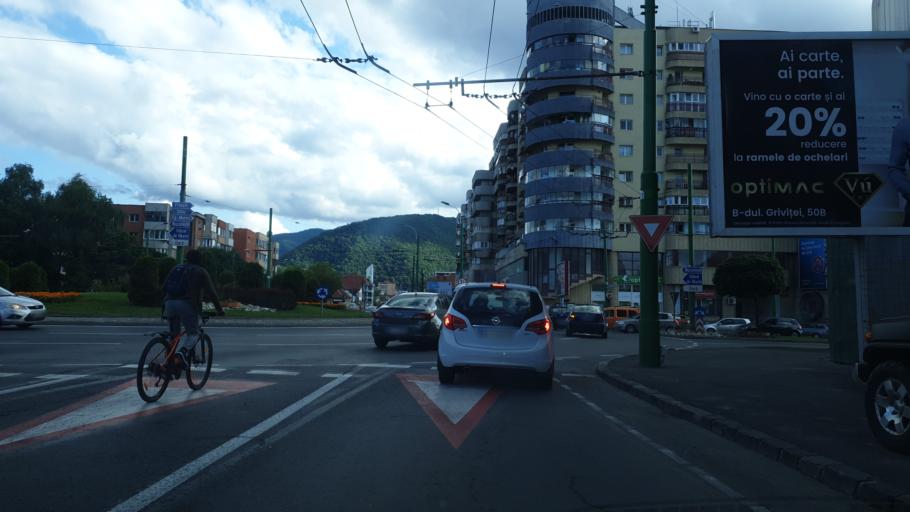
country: RO
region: Brasov
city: Brasov
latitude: 45.6601
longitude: 25.6071
